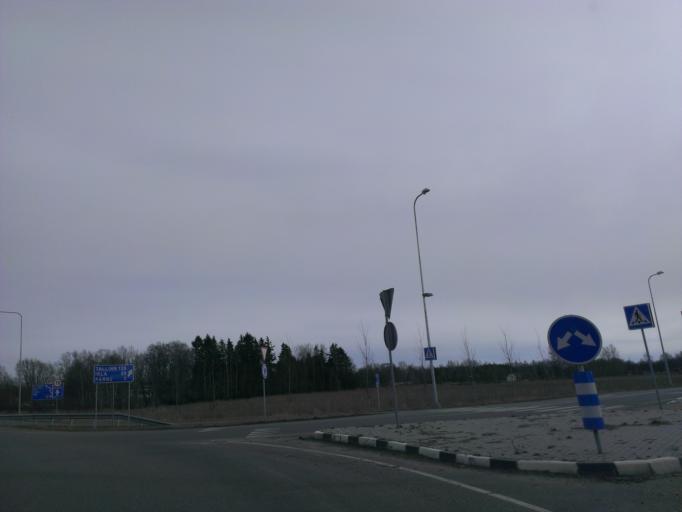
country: EE
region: Paernumaa
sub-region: Paernu linn
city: Parnu
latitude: 58.3970
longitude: 24.4478
